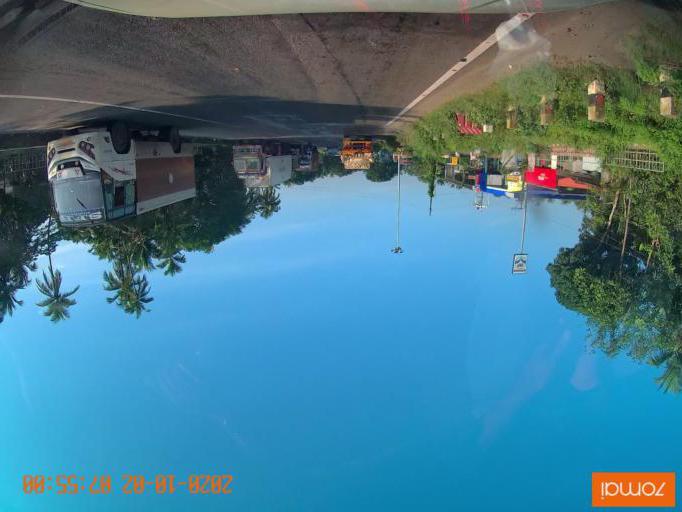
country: IN
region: Kerala
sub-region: Kozhikode
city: Ferokh
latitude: 11.1793
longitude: 75.8725
